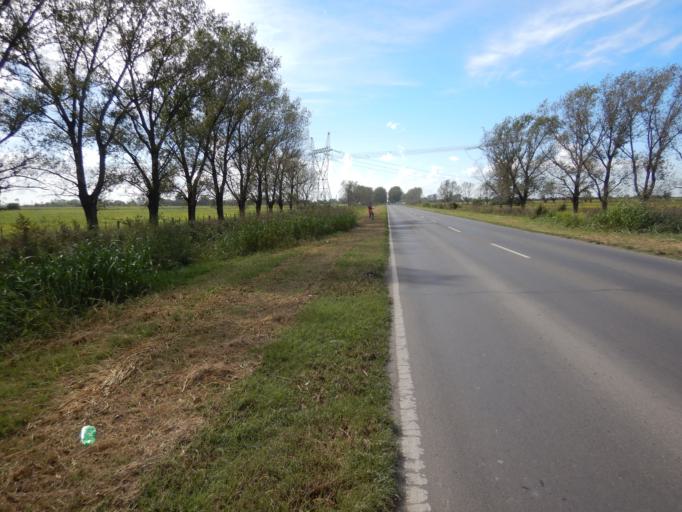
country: AR
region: Santa Fe
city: Roldan
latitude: -32.9006
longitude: -60.9362
